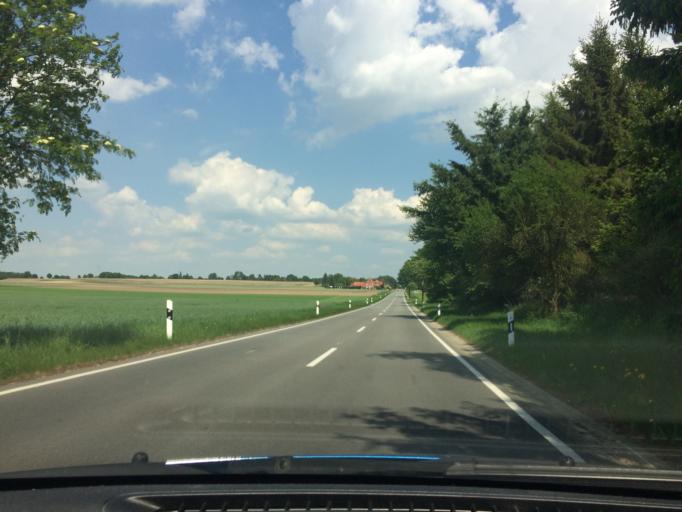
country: DE
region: Lower Saxony
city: Tosterglope
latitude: 53.2025
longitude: 10.8066
